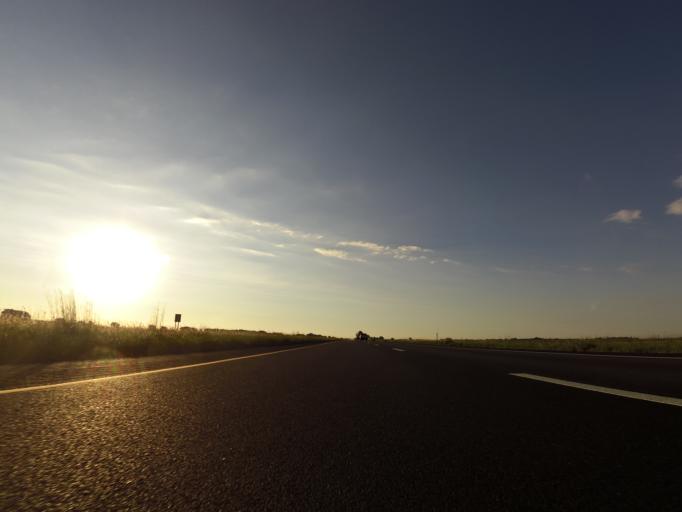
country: US
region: Kansas
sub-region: Sedgwick County
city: Colwich
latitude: 37.8518
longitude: -97.6036
